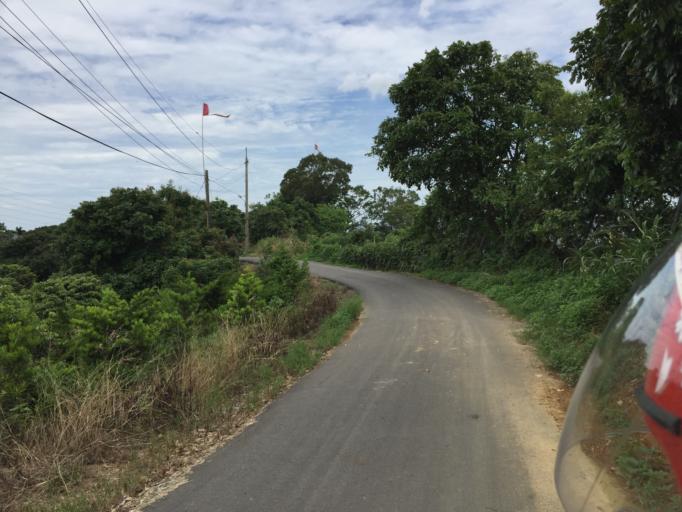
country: TW
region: Taiwan
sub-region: Taichung City
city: Taichung
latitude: 24.0637
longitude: 120.7192
